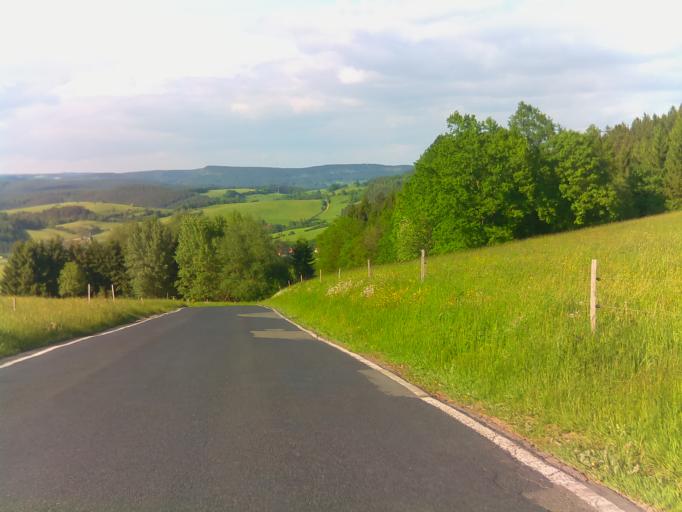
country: DE
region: Thuringia
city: Allendorf
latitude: 50.6424
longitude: 11.1472
